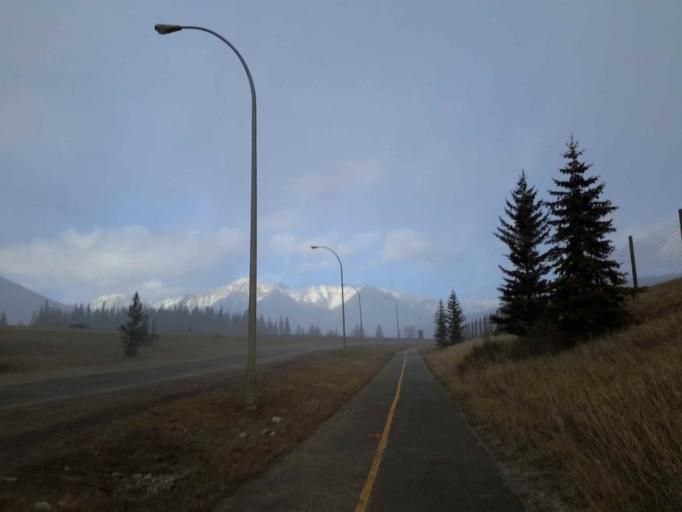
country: CA
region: Alberta
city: Banff
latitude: 51.2074
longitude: -115.5365
